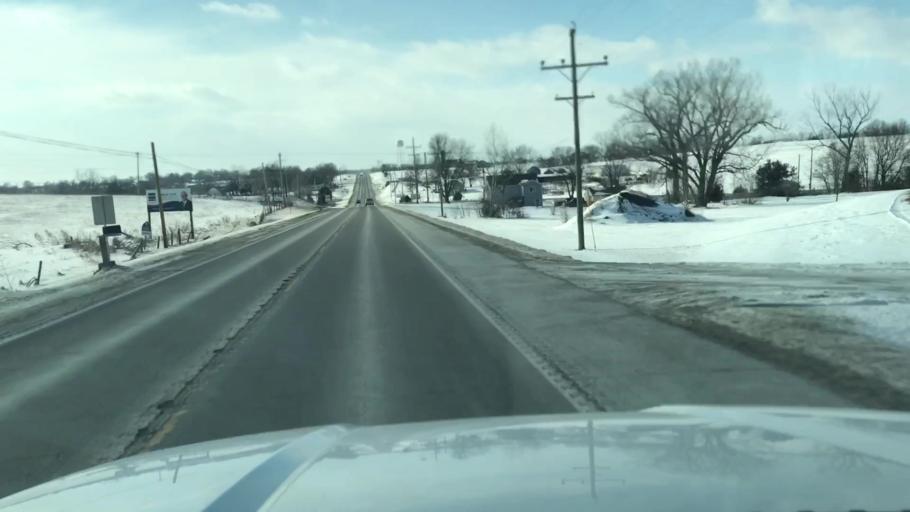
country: US
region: Missouri
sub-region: Nodaway County
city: Maryville
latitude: 40.3446
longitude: -94.7962
